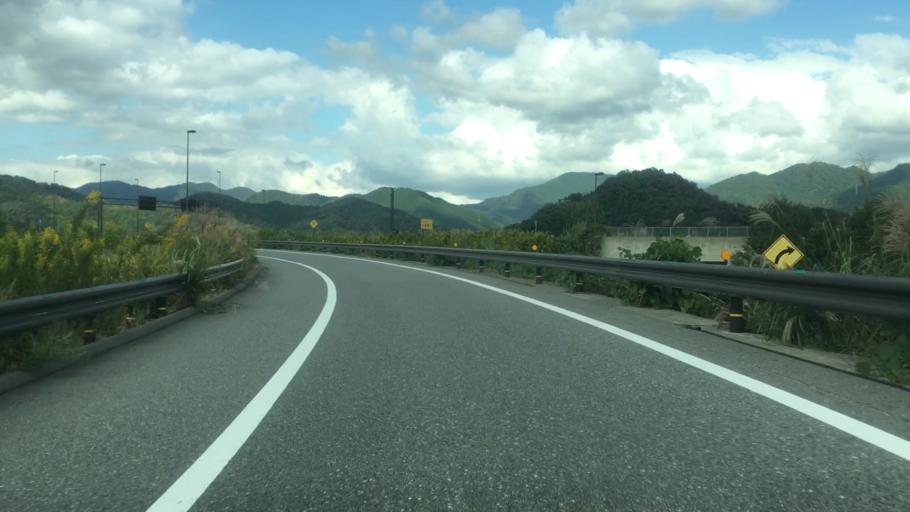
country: JP
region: Hyogo
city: Toyooka
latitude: 35.3149
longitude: 134.8454
